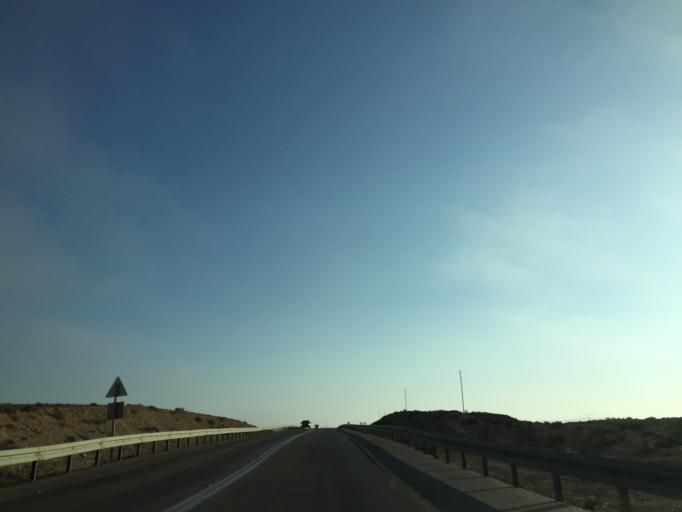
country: IL
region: Southern District
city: Yeroham
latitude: 30.9966
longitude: 34.9269
